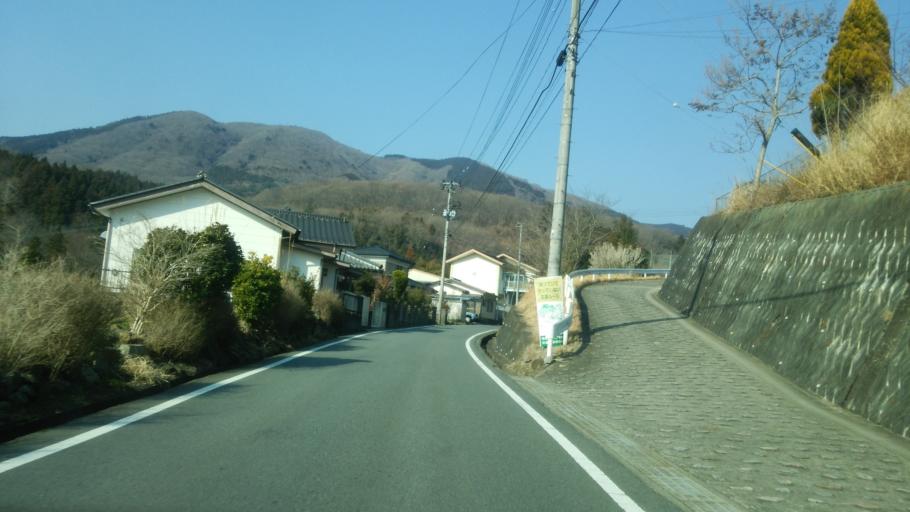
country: JP
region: Fukushima
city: Iwaki
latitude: 37.0290
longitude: 140.8187
